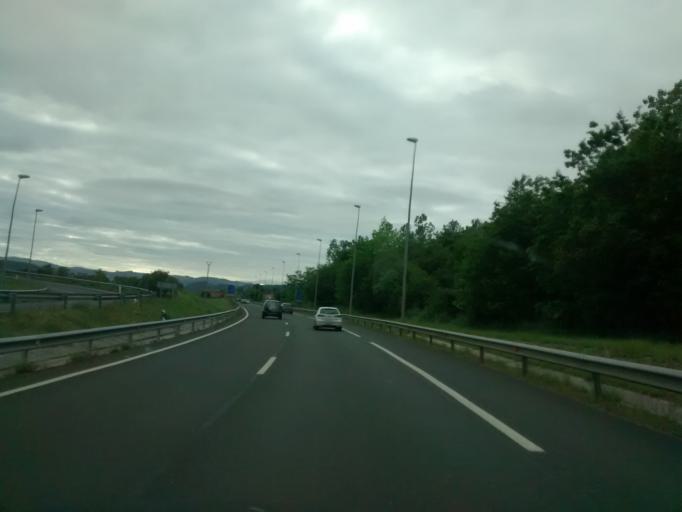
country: ES
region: Cantabria
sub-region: Provincia de Cantabria
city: Torrelavega
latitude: 43.3488
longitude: -4.0293
